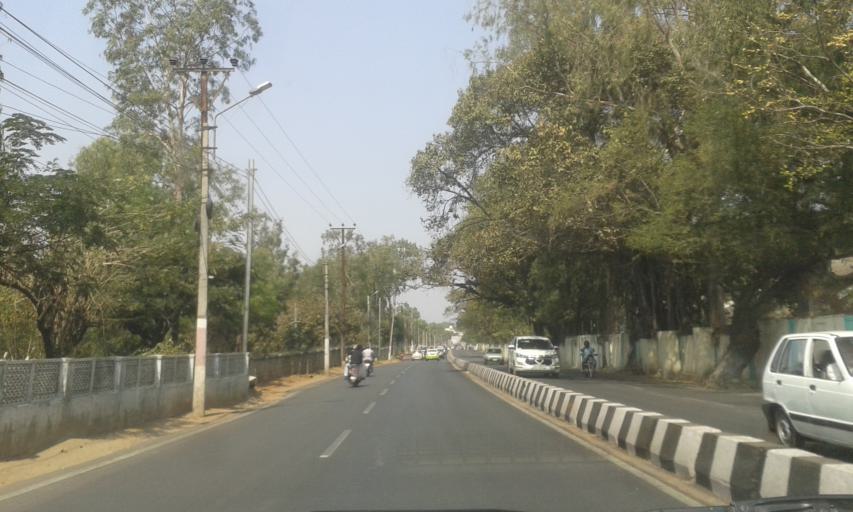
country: IN
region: Telangana
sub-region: Rangareddi
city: Secunderabad
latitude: 17.4855
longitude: 78.5116
